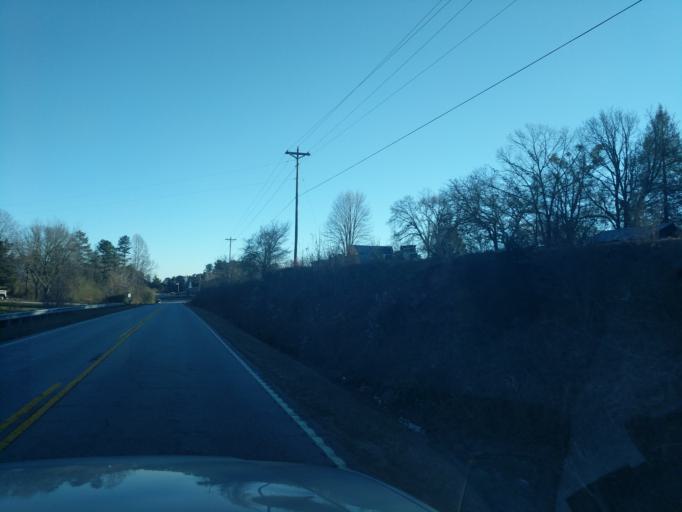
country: US
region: South Carolina
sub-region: Oconee County
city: Westminster
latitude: 34.7065
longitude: -83.1942
